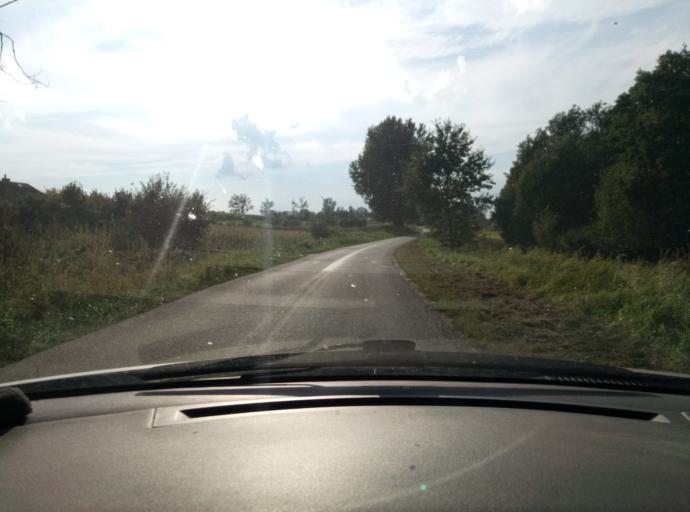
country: PL
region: Kujawsko-Pomorskie
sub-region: Powiat brodnicki
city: Jablonowo Pomorskie
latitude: 53.3869
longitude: 19.2170
